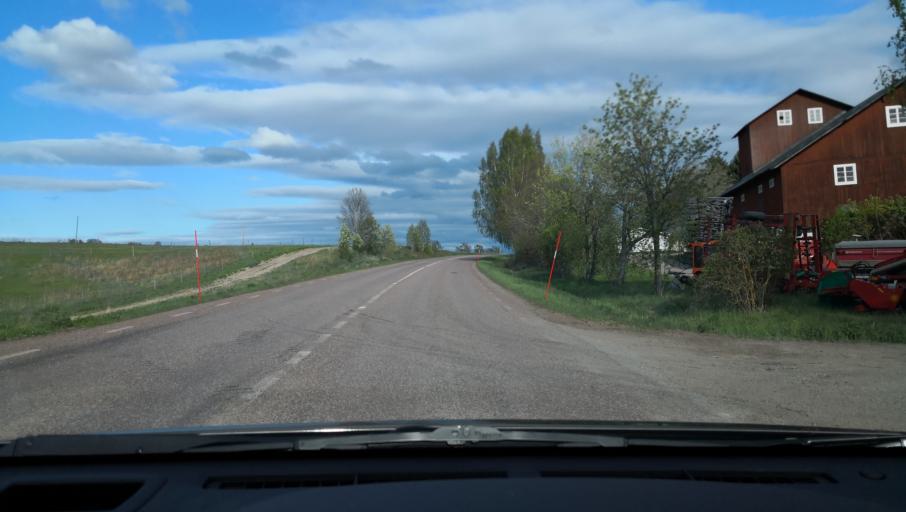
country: SE
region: Dalarna
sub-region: Hedemora Kommun
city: Hedemora
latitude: 60.2847
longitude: 15.9378
